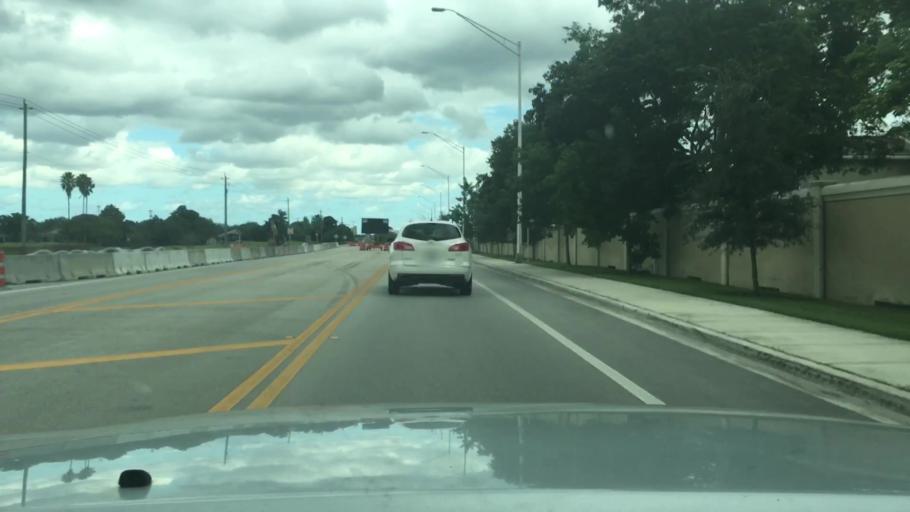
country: US
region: Florida
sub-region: Miami-Dade County
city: Country Club
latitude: 25.9931
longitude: -80.3490
